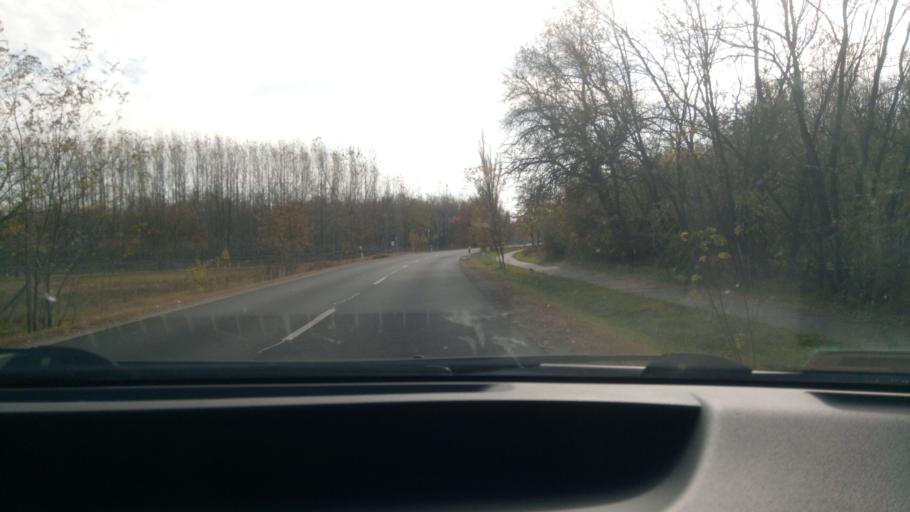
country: HU
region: Bacs-Kiskun
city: Jaszszentlaszlo
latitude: 46.5343
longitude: 19.7393
